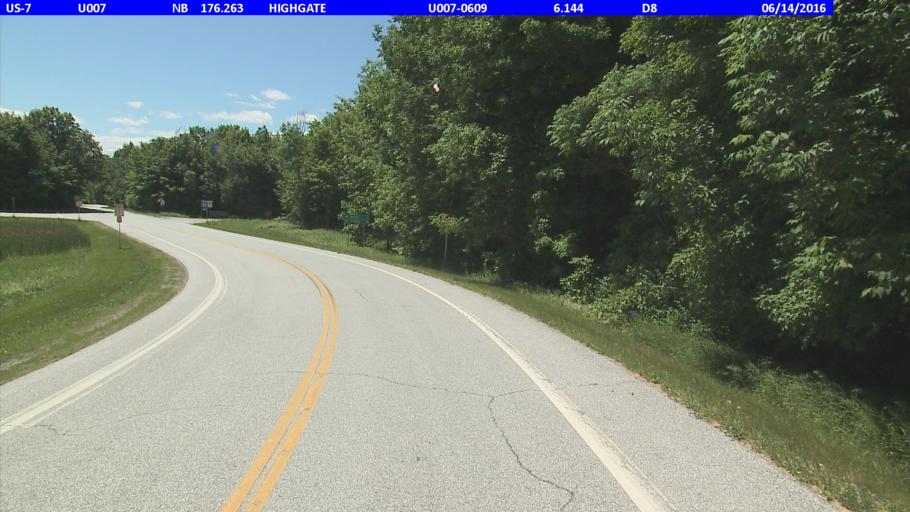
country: US
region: Vermont
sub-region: Franklin County
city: Swanton
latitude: 45.0087
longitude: -73.0882
